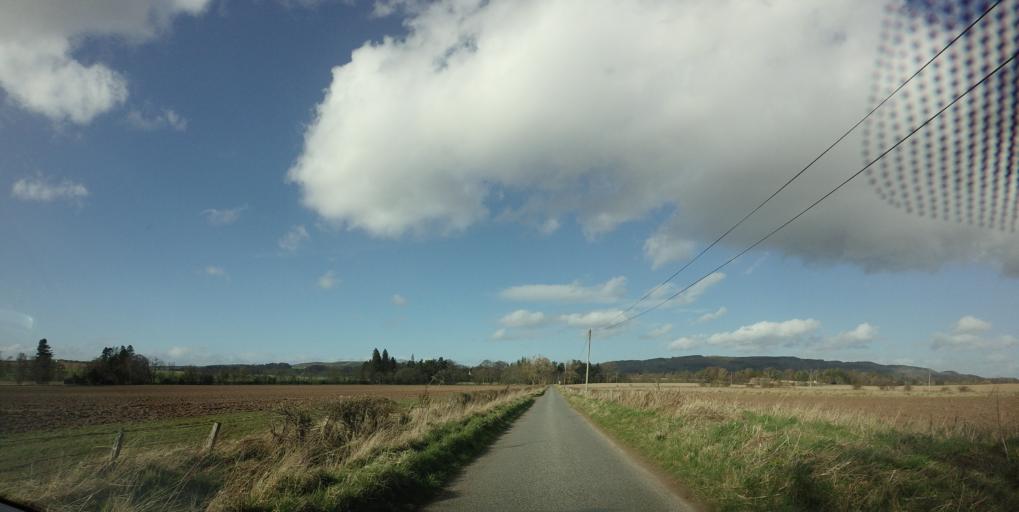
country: GB
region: Scotland
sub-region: Perth and Kinross
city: Bridge of Earn
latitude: 56.3330
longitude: -3.4295
